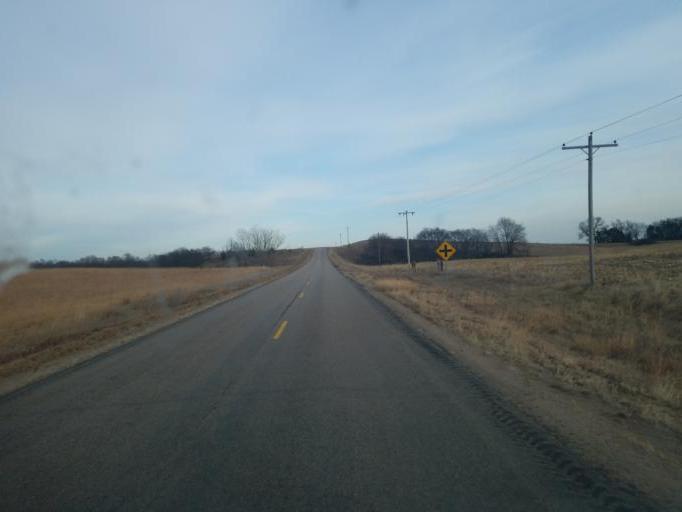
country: US
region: Nebraska
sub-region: Knox County
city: Creighton
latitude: 42.4662
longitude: -98.1541
